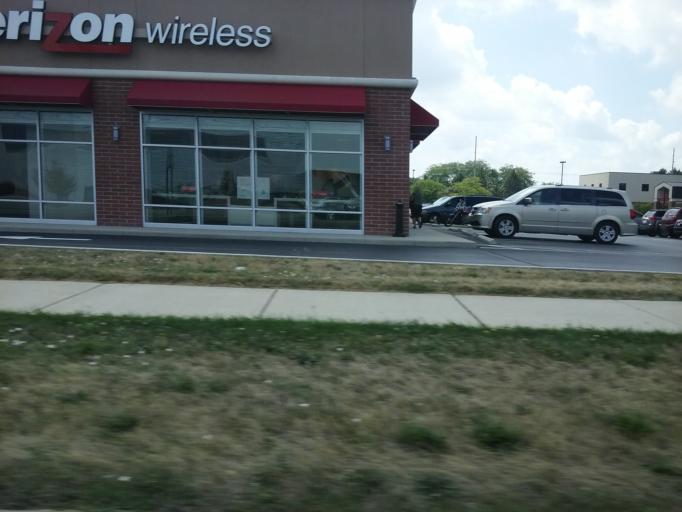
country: US
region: Ohio
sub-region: Wood County
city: Bowling Green
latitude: 41.3745
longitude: -83.6265
